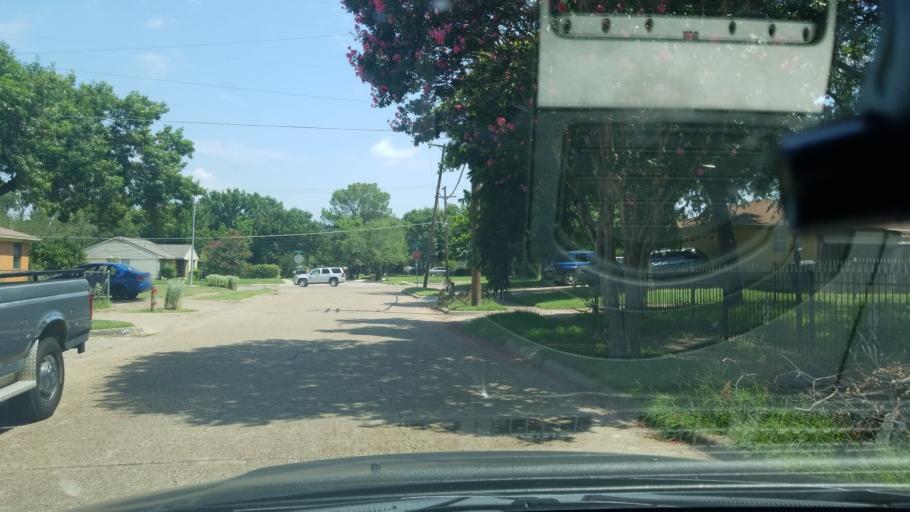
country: US
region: Texas
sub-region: Dallas County
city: Balch Springs
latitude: 32.7483
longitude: -96.6856
